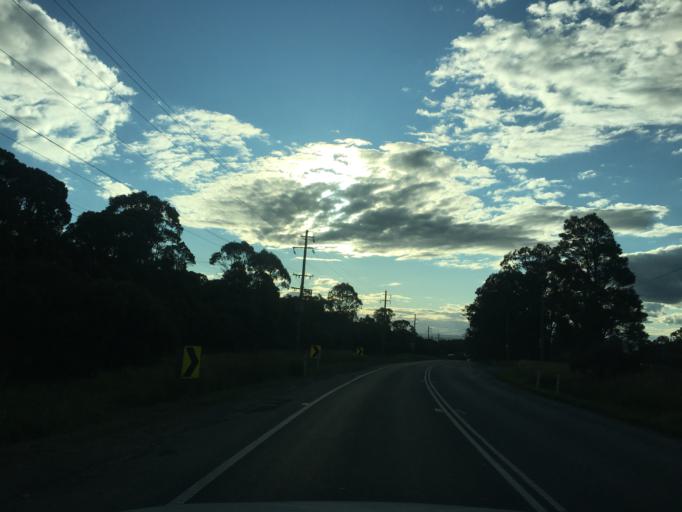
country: AU
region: New South Wales
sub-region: Fairfield
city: Cecil Park
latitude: -33.8794
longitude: 150.7851
